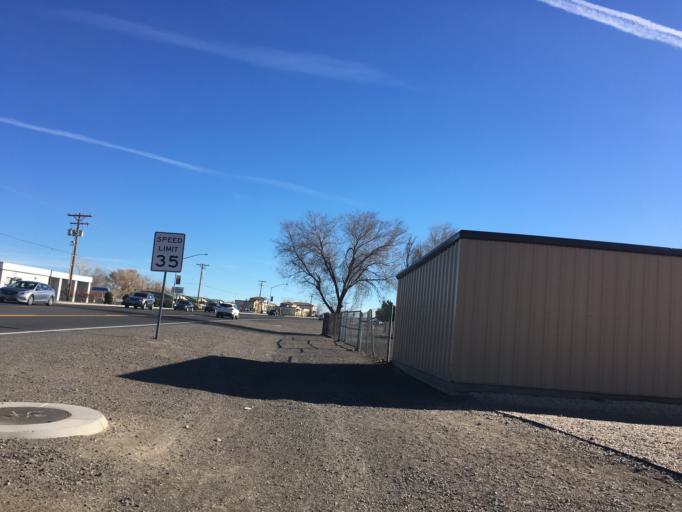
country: US
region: Nevada
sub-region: Lyon County
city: Fernley
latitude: 39.6075
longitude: -119.2454
